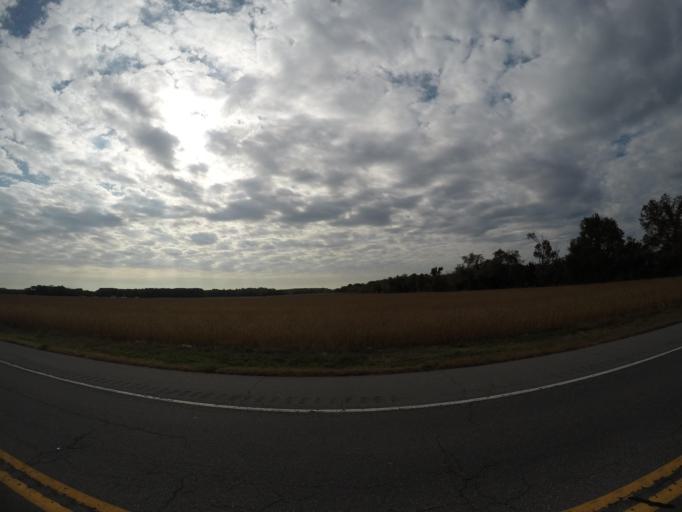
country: US
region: Delaware
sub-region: Sussex County
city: Lewes
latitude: 38.7396
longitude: -75.2020
